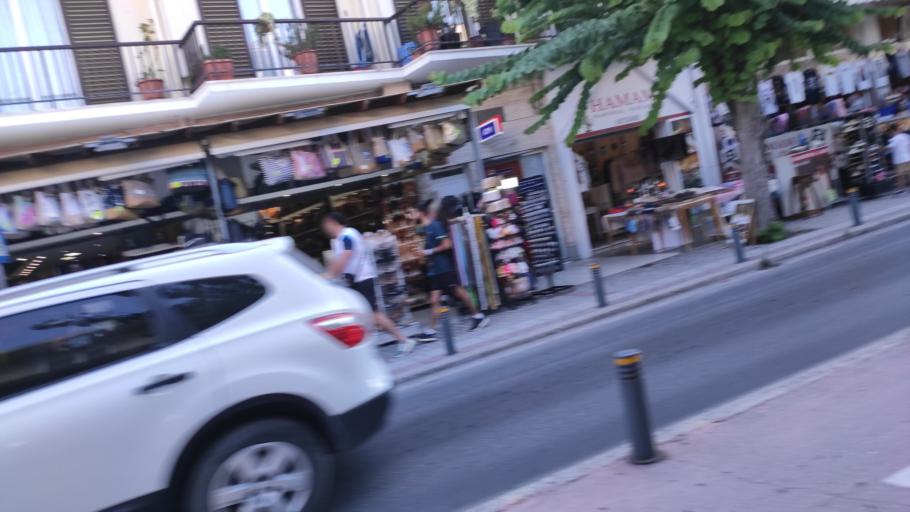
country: GR
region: South Aegean
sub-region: Nomos Dodekanisou
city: Kos
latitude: 36.8976
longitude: 27.2849
